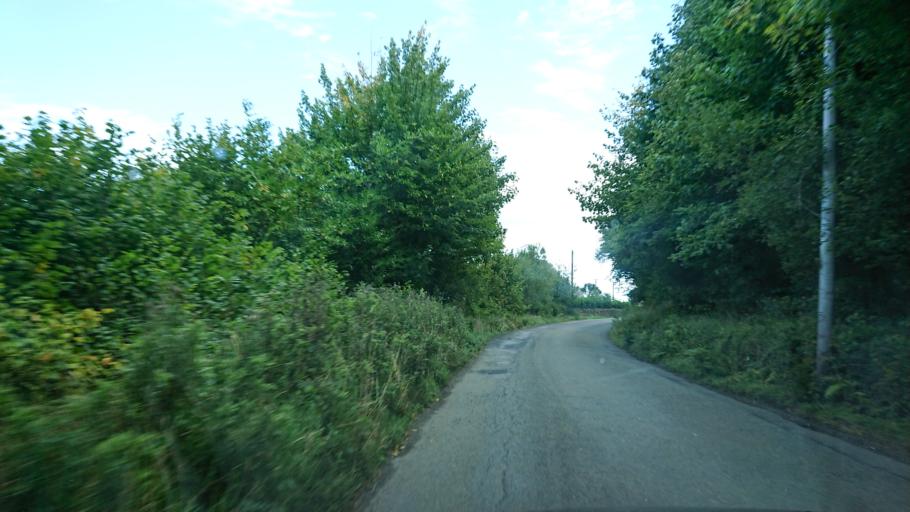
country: IE
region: Munster
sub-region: Waterford
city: Dungarvan
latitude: 52.1219
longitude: -7.6885
